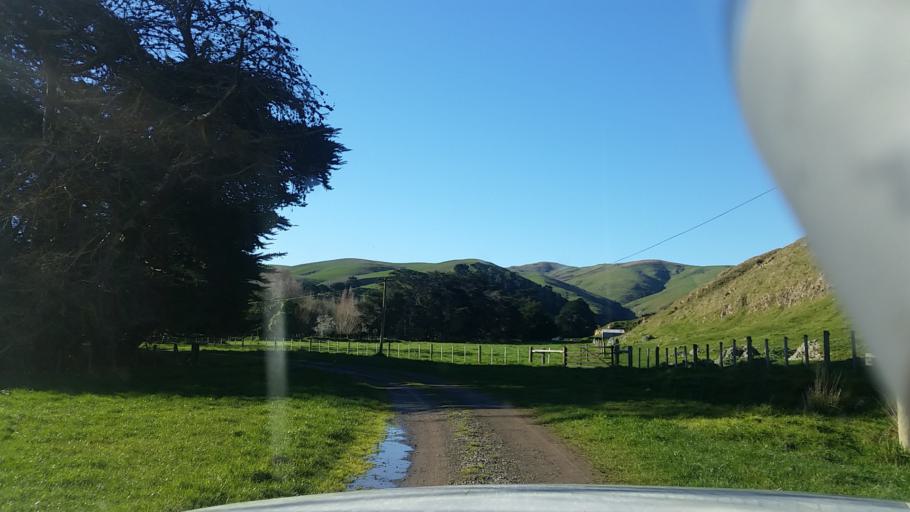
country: NZ
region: Canterbury
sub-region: Selwyn District
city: Lincoln
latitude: -43.7890
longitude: 172.6652
